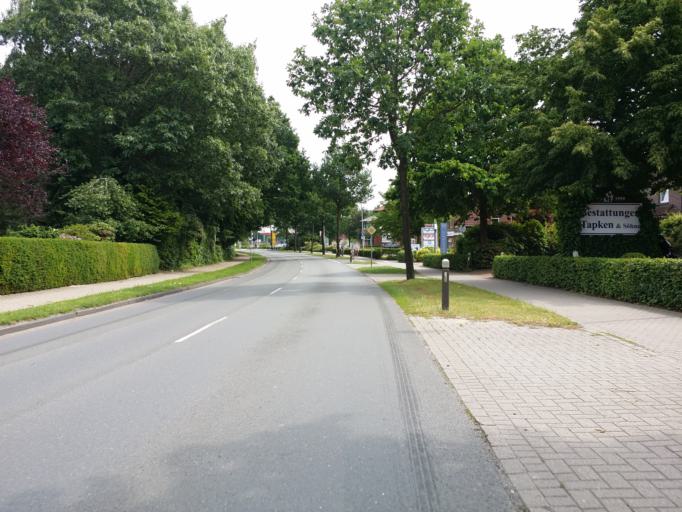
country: DE
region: Lower Saxony
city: Wiefelstede
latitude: 53.2520
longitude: 8.1182
